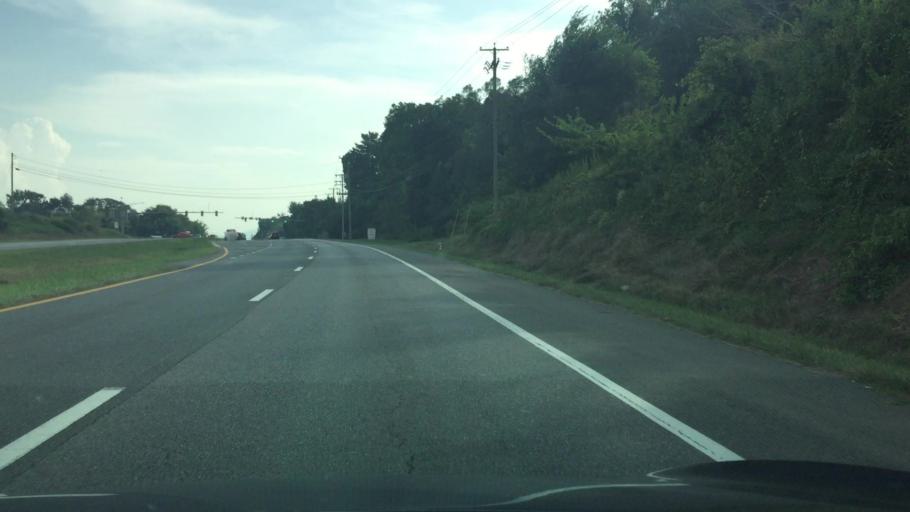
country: US
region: Virginia
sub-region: Roanoke County
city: Vinton
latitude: 37.3148
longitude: -79.8818
